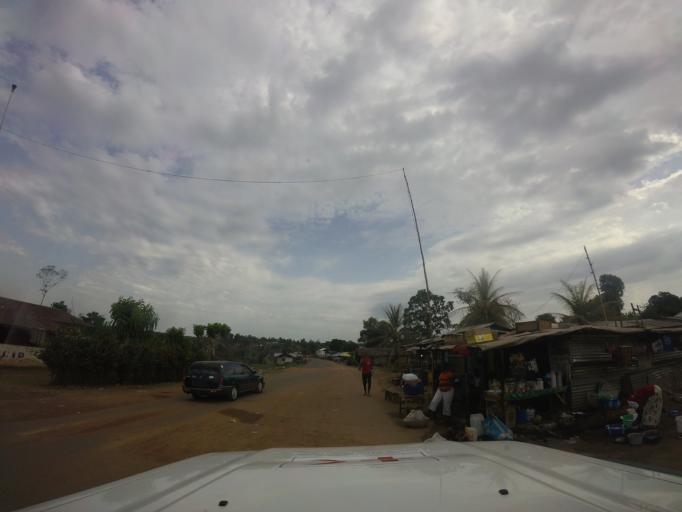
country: LR
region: Grand Cape Mount
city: Robertsport
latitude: 6.8168
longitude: -11.1369
